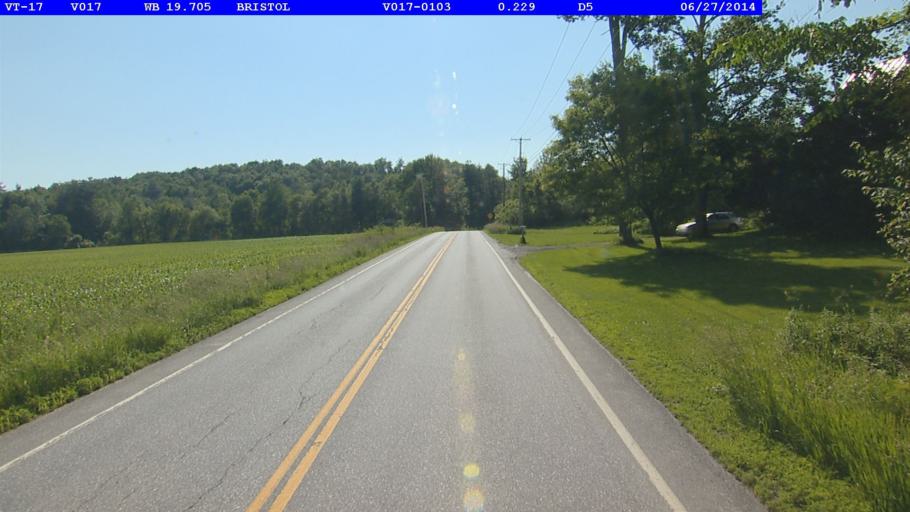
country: US
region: Vermont
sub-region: Addison County
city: Bristol
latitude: 44.1287
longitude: -73.1046
